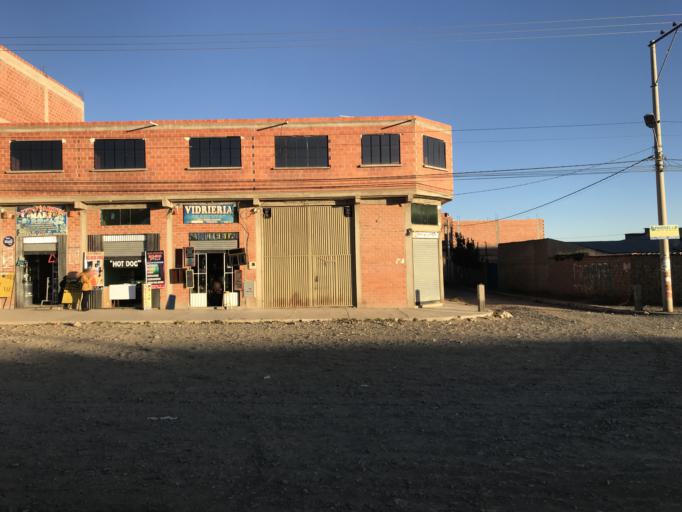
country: BO
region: La Paz
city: La Paz
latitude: -16.5029
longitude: -68.2449
